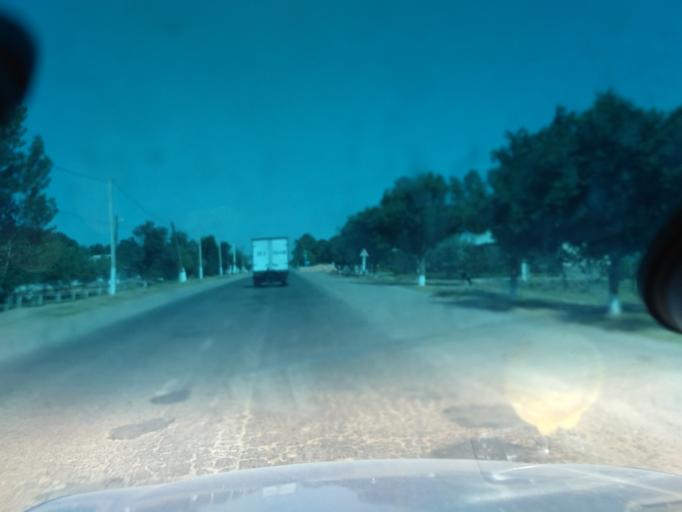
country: UZ
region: Sirdaryo
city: Guliston
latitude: 40.4874
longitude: 68.8847
